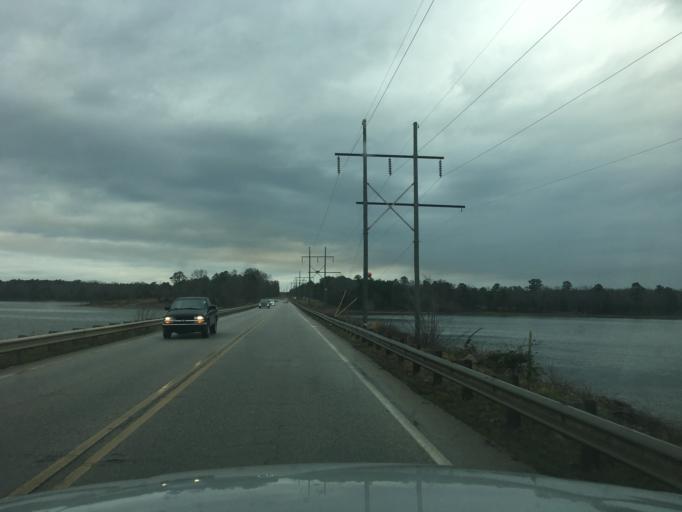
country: US
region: Georgia
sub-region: Columbia County
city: Appling
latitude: 33.7004
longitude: -82.3437
